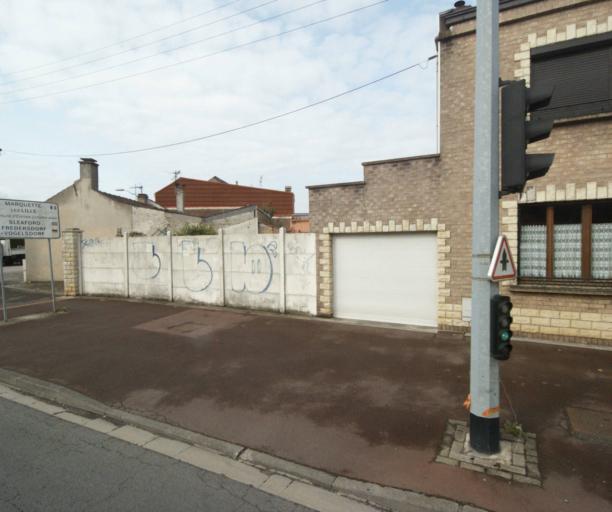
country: FR
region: Nord-Pas-de-Calais
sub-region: Departement du Nord
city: Wambrechies
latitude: 50.6754
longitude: 3.0496
